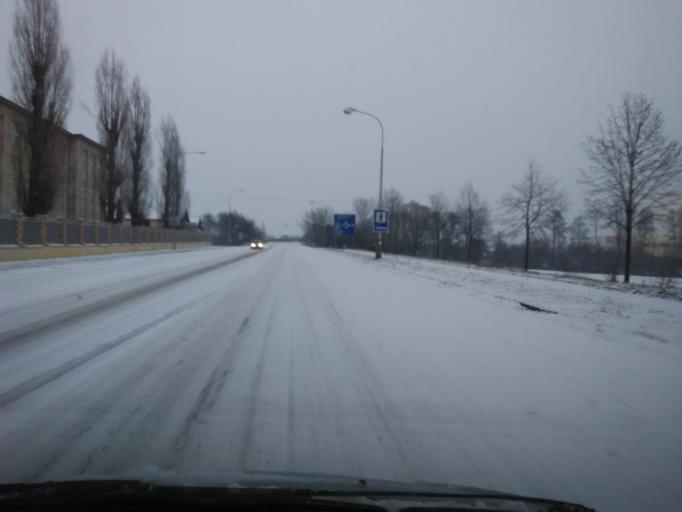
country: CZ
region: Olomoucky
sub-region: Okres Prerov
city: Lipnik nad Becvou
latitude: 49.5296
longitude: 17.6025
